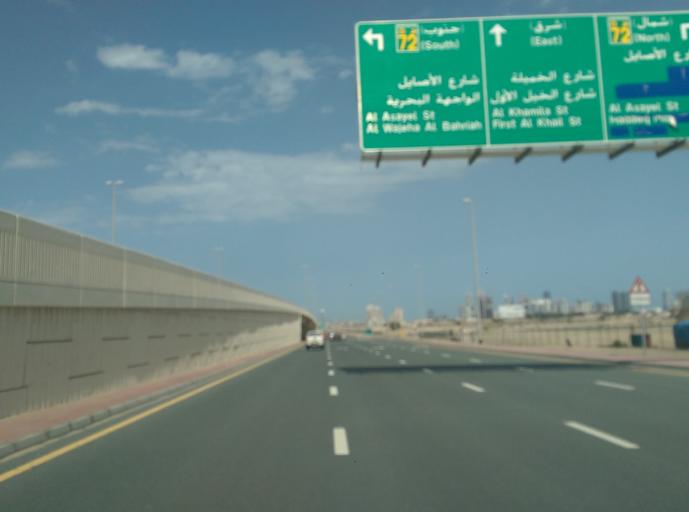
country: AE
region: Dubai
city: Dubai
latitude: 25.0667
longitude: 55.1950
